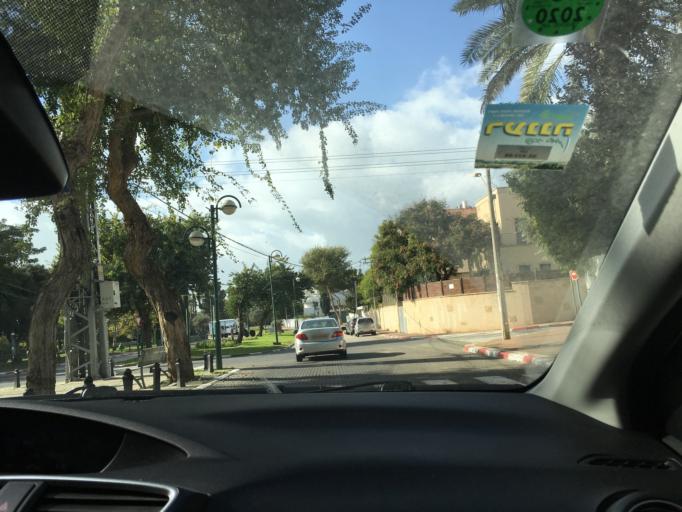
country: IL
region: Tel Aviv
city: Ramat HaSharon
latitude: 32.1471
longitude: 34.8350
